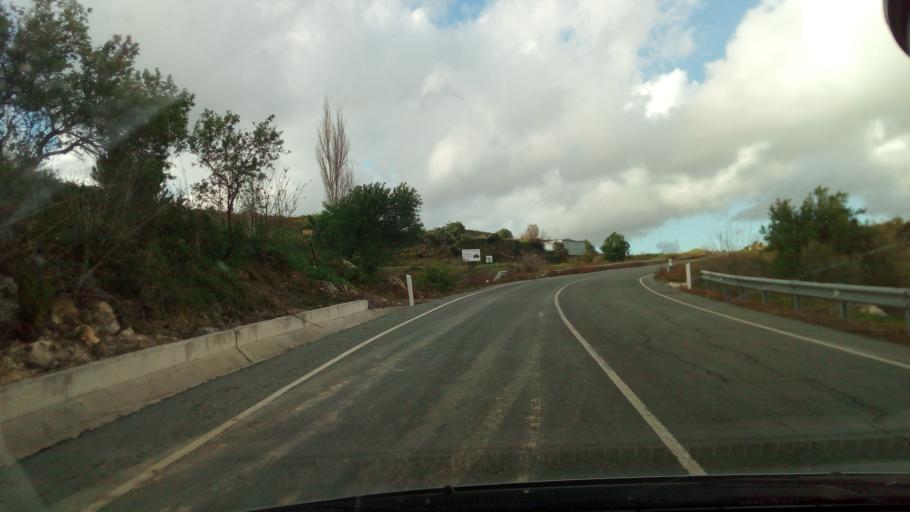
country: CY
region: Pafos
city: Mesogi
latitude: 34.8602
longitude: 32.5033
